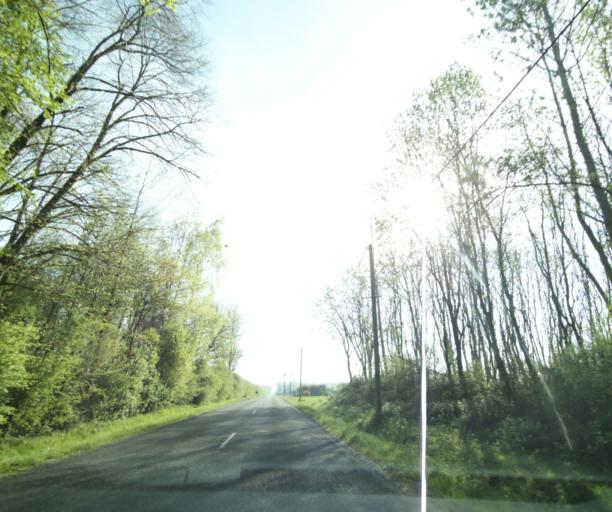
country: FR
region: Ile-de-France
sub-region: Departement de Seine-et-Marne
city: La Chapelle-Gauthier
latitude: 48.5133
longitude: 2.9380
